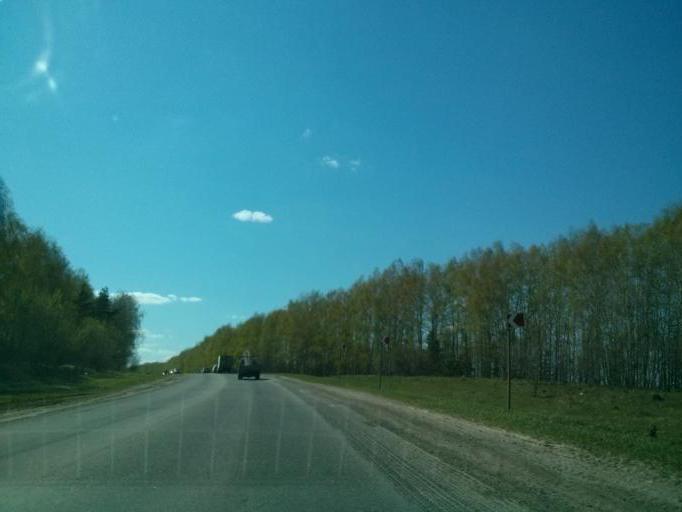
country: RU
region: Nizjnij Novgorod
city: Pavlovo
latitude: 55.9630
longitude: 43.1817
